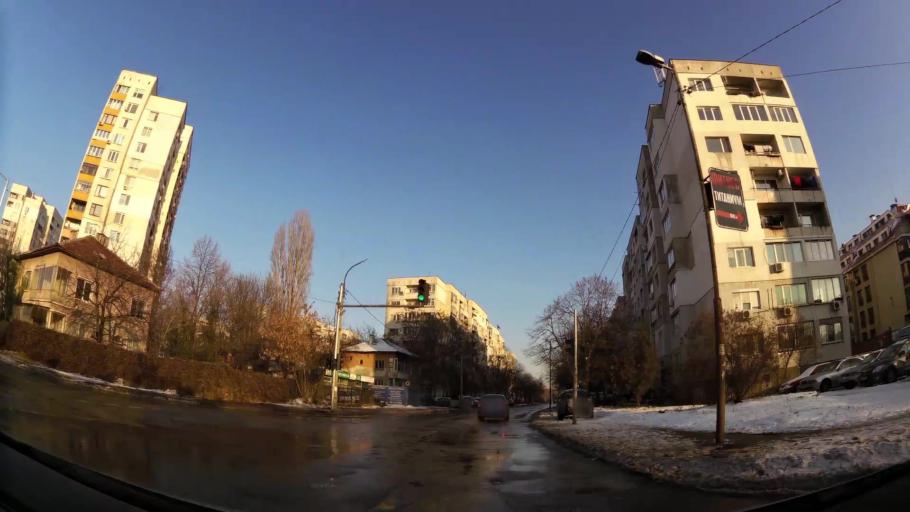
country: BG
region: Sofia-Capital
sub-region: Stolichna Obshtina
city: Sofia
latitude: 42.6803
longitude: 23.3749
